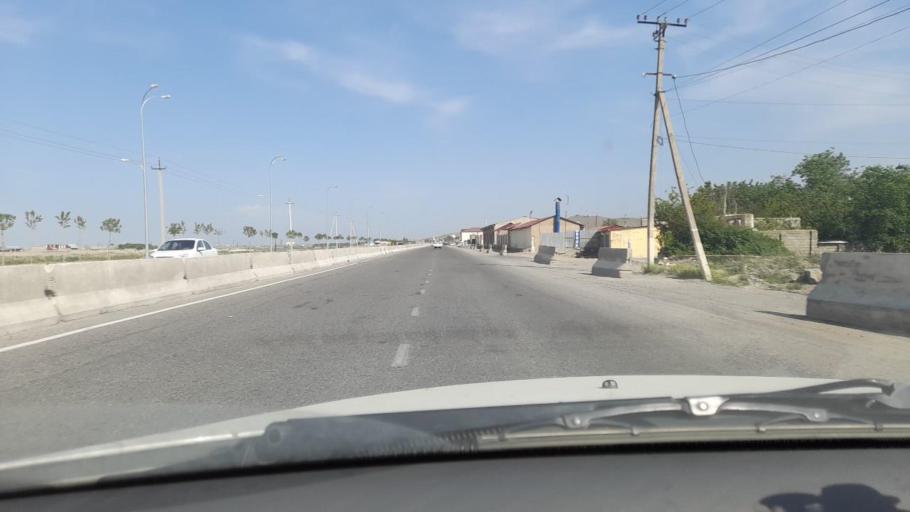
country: UZ
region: Samarqand
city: Samarqand
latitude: 39.7050
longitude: 66.9983
